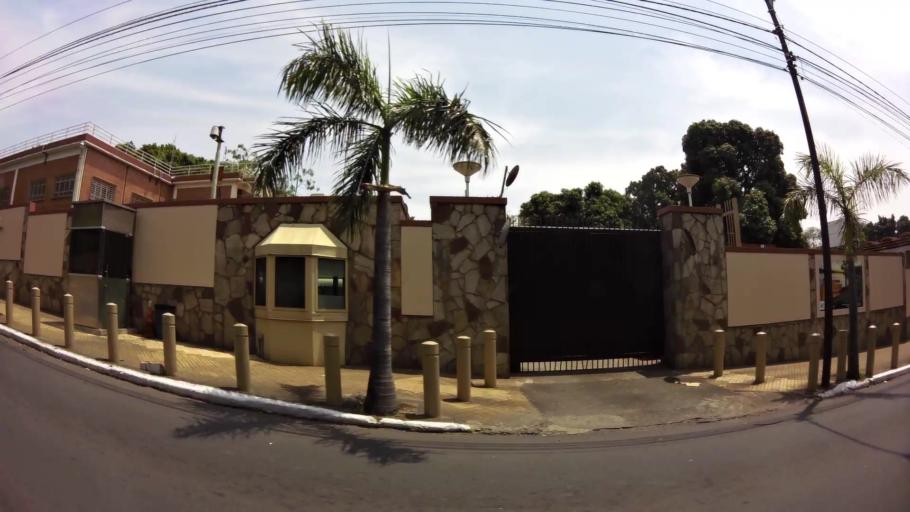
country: PY
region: Asuncion
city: Asuncion
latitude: -25.2942
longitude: -57.6043
